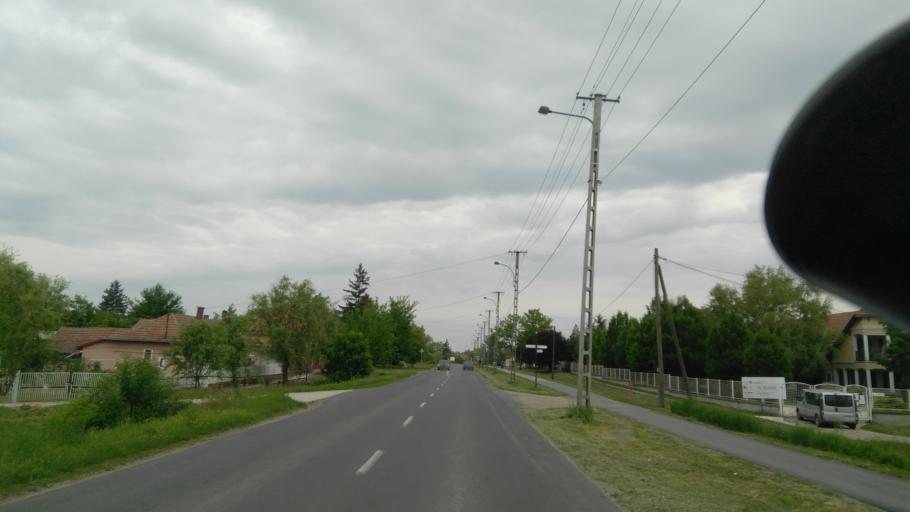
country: HU
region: Bekes
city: Veszto
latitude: 46.9095
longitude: 21.2583
